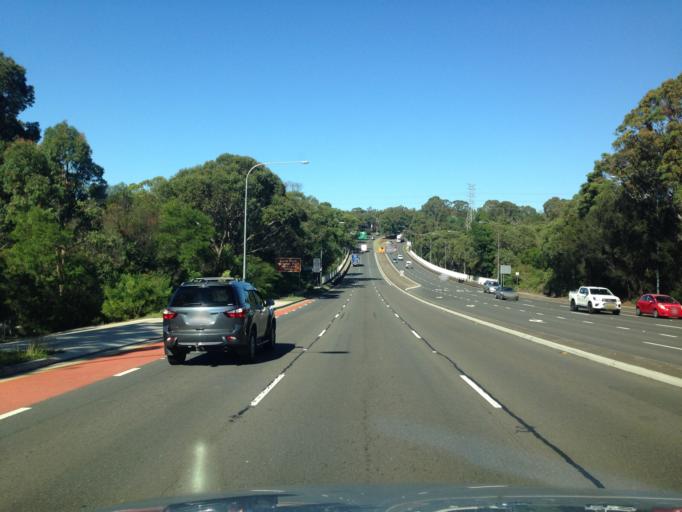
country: AU
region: New South Wales
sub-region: Ryde
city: Macquarie Park
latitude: -33.7739
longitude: 151.1355
